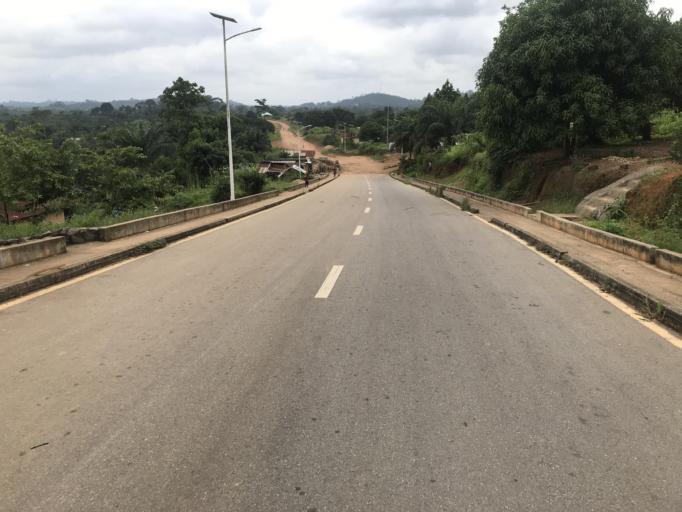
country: SL
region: Eastern Province
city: Kailahun
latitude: 8.2873
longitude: -10.5598
